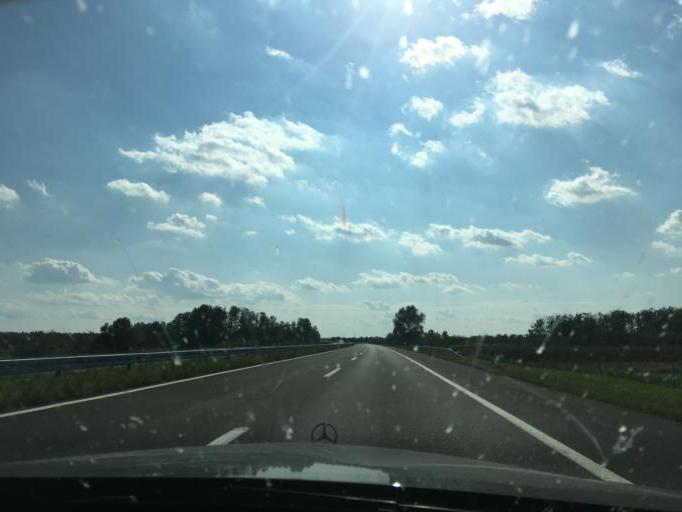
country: HR
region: Medimurska
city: Palovec
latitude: 46.3955
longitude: 16.5667
